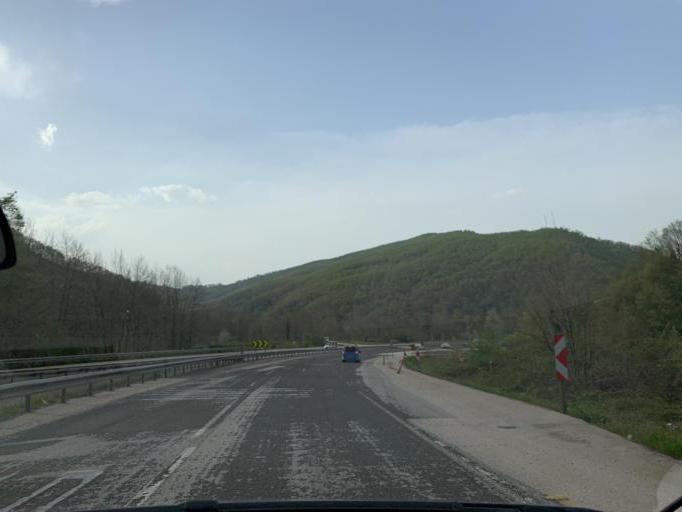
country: TR
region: Bursa
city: Tahtakopru
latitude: 39.9909
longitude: 29.6516
